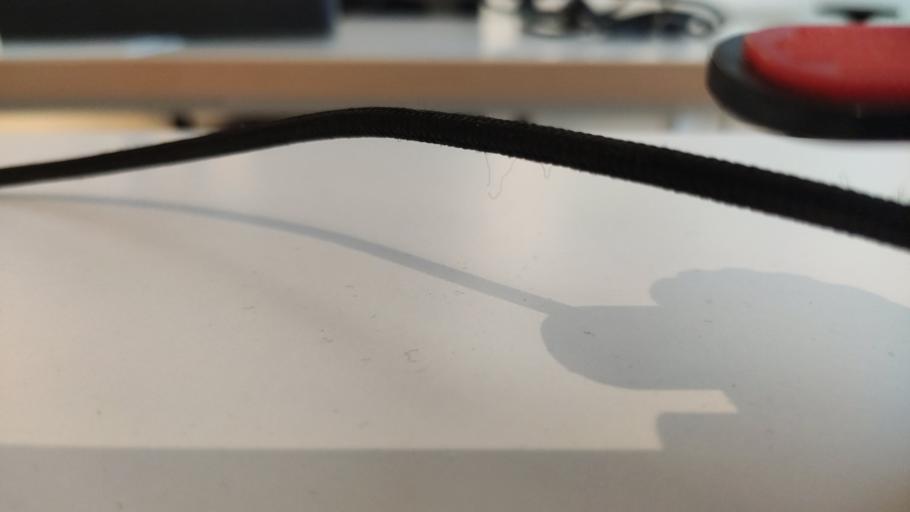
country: RU
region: Moskovskaya
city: Novopetrovskoye
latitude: 55.9598
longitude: 36.4394
